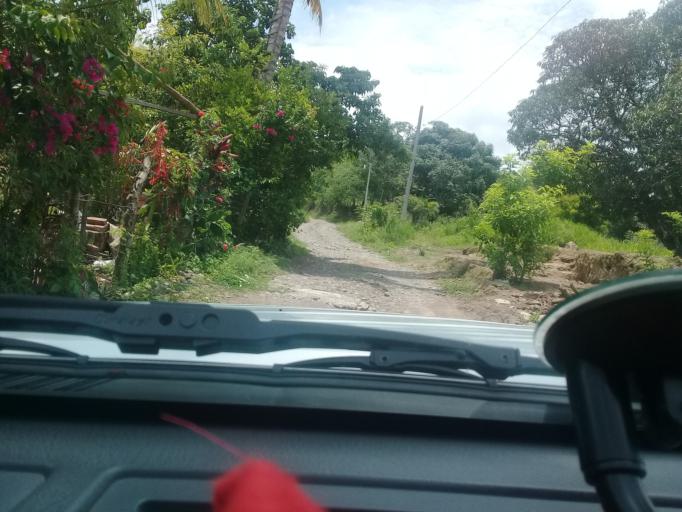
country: MX
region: Veracruz
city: Paso de Ovejas
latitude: 19.2782
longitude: -96.4313
